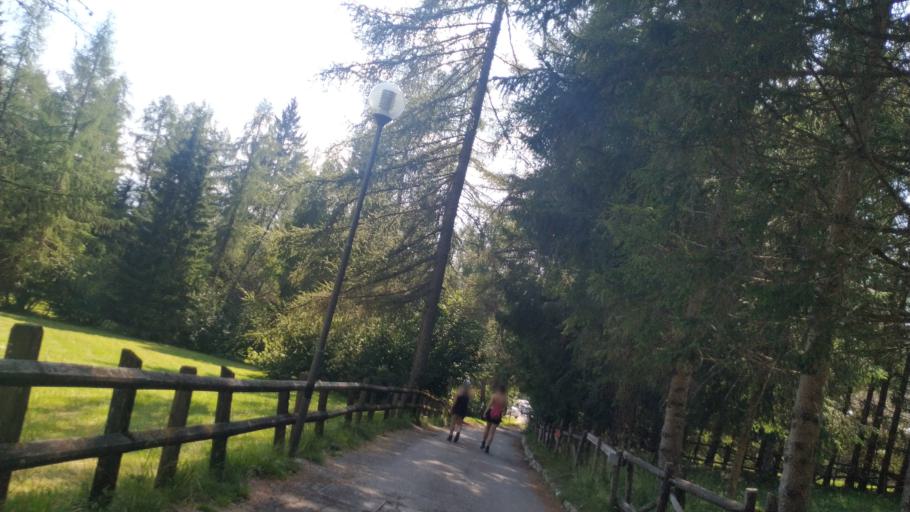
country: IT
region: Trentino-Alto Adige
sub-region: Bolzano
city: San Felice
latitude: 46.4834
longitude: 11.1500
